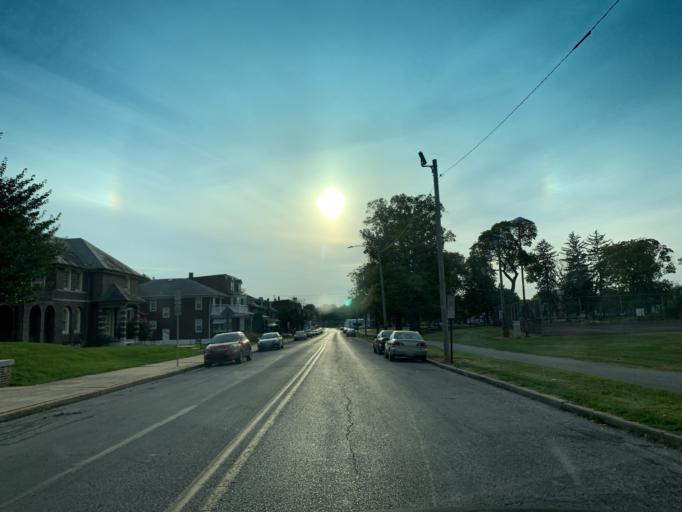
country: US
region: Pennsylvania
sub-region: York County
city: York
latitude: 39.9555
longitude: -76.7261
